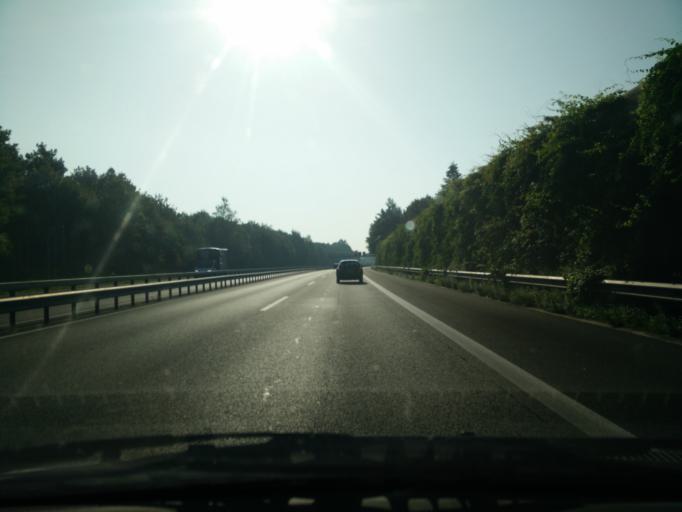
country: DE
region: Schleswig-Holstein
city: Halstenbek
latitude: 53.6341
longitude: 9.8549
